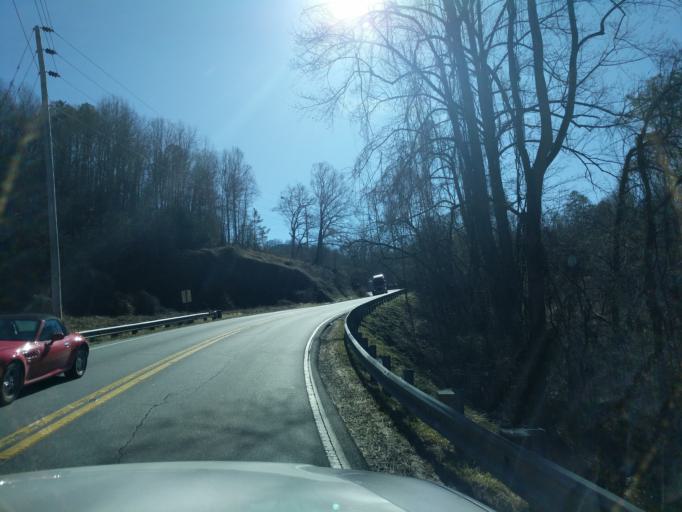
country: US
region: North Carolina
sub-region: Swain County
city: Bryson City
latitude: 35.3611
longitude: -83.5537
